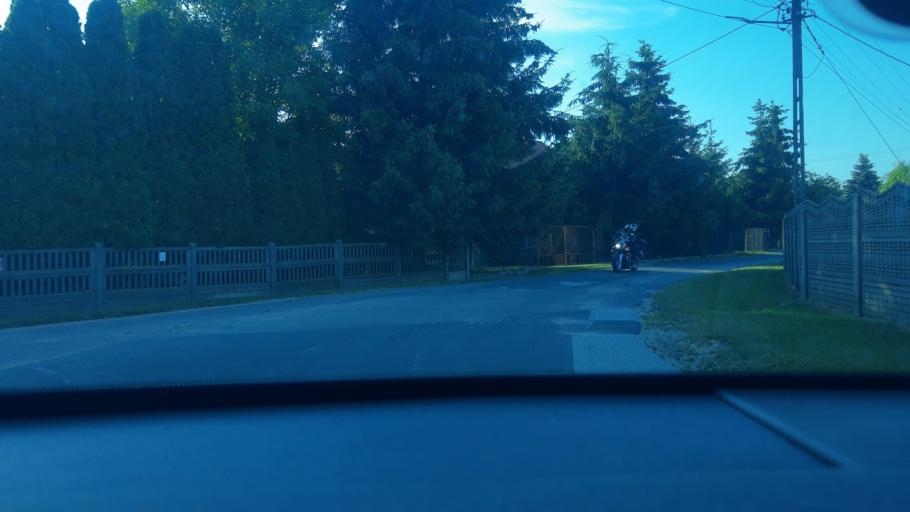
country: PL
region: Lodz Voivodeship
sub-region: Powiat sieradzki
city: Sieradz
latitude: 51.5442
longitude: 18.7543
